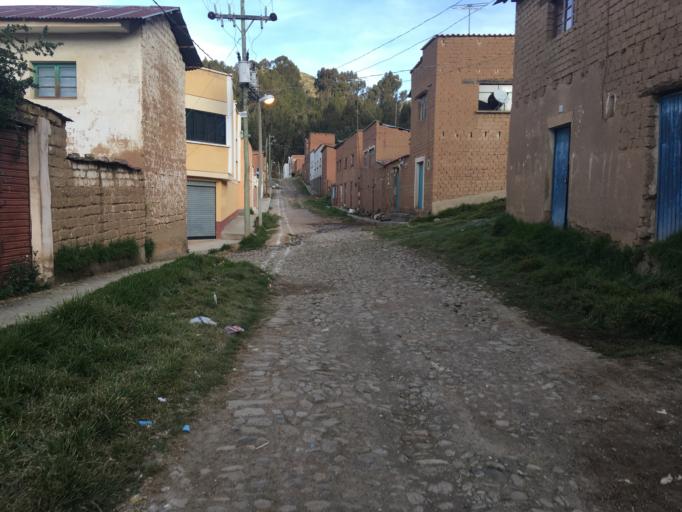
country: BO
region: La Paz
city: San Pedro
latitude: -16.2232
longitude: -68.8530
